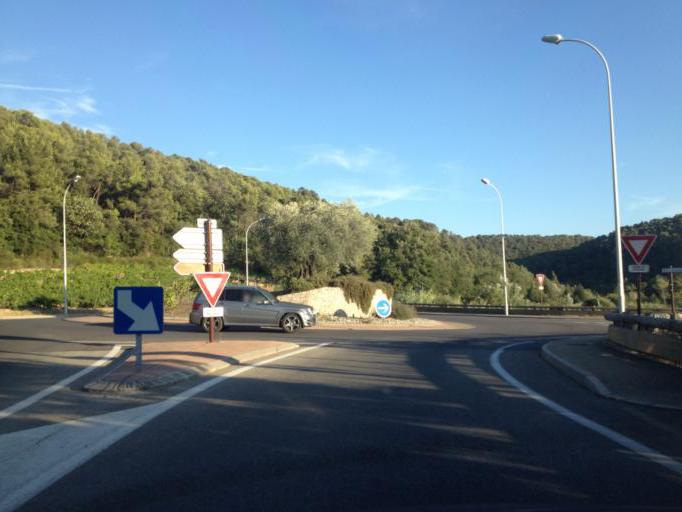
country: FR
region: Provence-Alpes-Cote d'Azur
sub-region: Departement du Vaucluse
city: Vaison-la-Romaine
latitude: 44.2457
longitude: 5.0481
